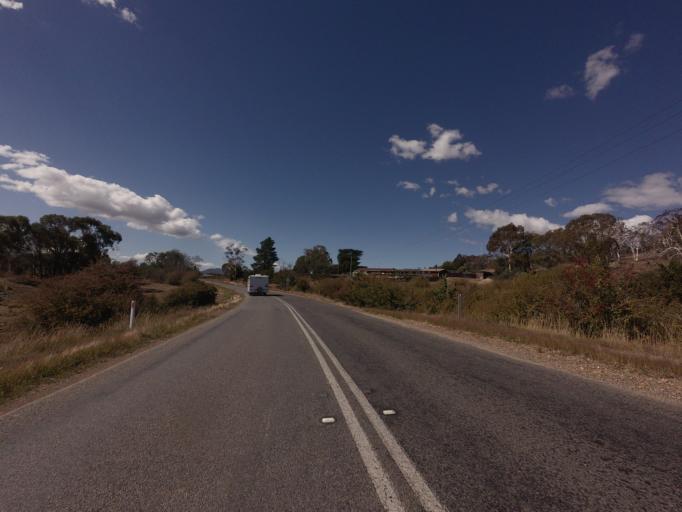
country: AU
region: Tasmania
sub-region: Break O'Day
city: St Helens
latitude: -41.6456
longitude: 147.9599
